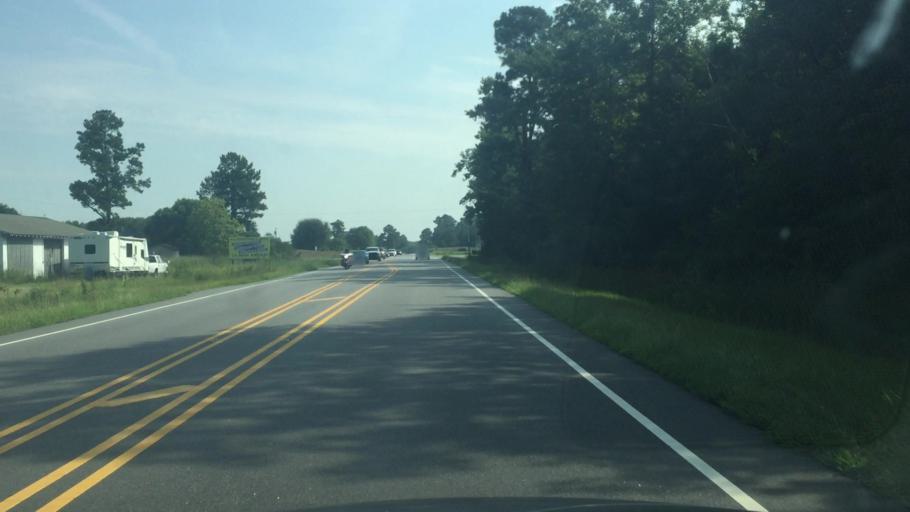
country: US
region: North Carolina
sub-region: Columbus County
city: Tabor City
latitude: 34.2007
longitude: -78.8327
